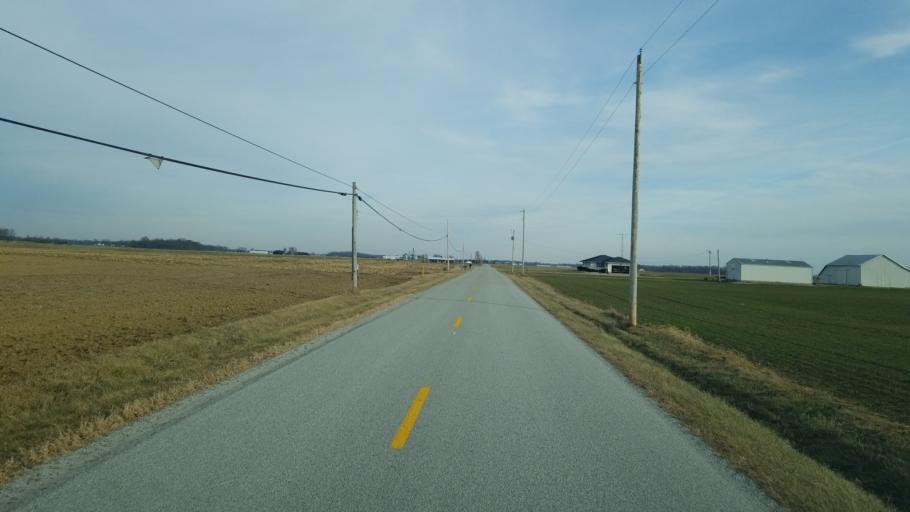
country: US
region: Ohio
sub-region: Hardin County
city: Kenton
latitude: 40.6584
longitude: -83.5340
